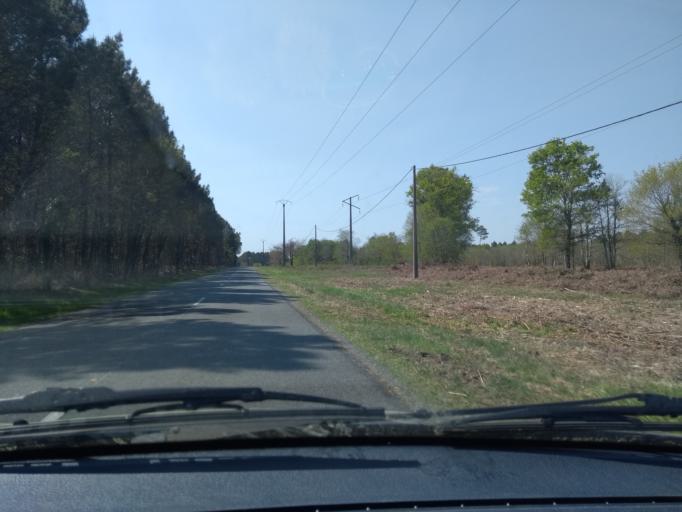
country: FR
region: Aquitaine
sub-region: Departement de la Gironde
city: Belin-Beliet
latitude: 44.5273
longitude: -0.7252
